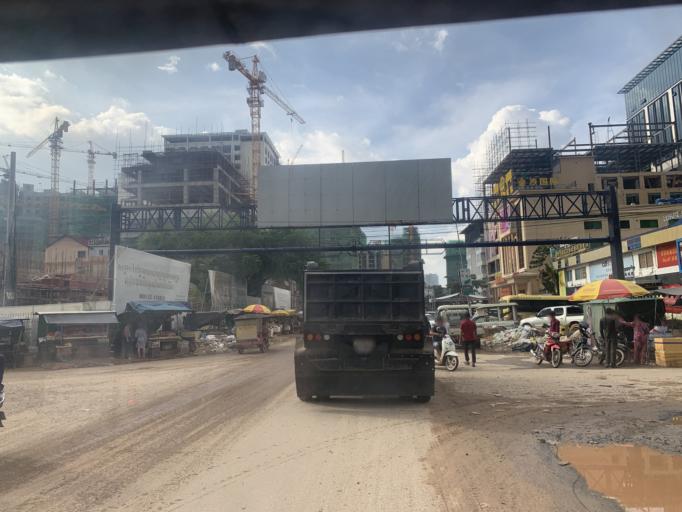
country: KH
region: Preah Sihanouk
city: Sihanoukville
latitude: 10.6077
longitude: 103.5251
